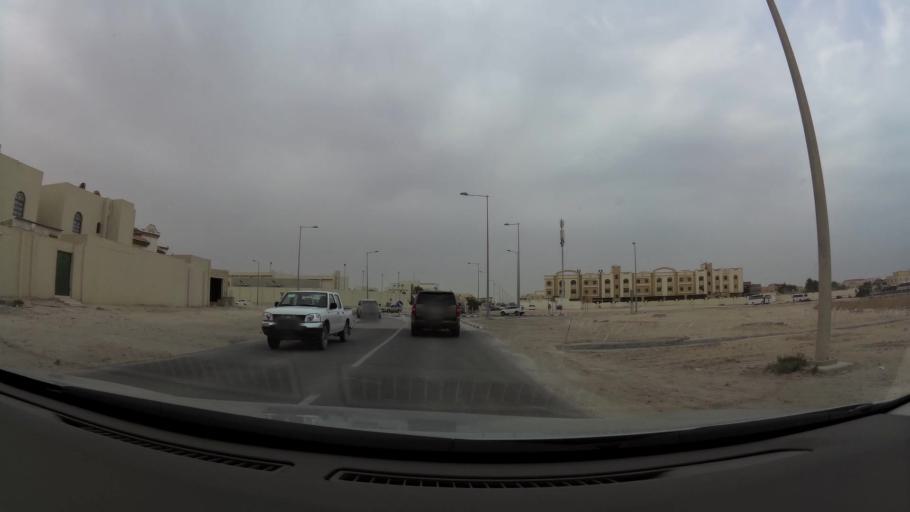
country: QA
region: Baladiyat ar Rayyan
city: Ar Rayyan
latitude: 25.3417
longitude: 51.4708
